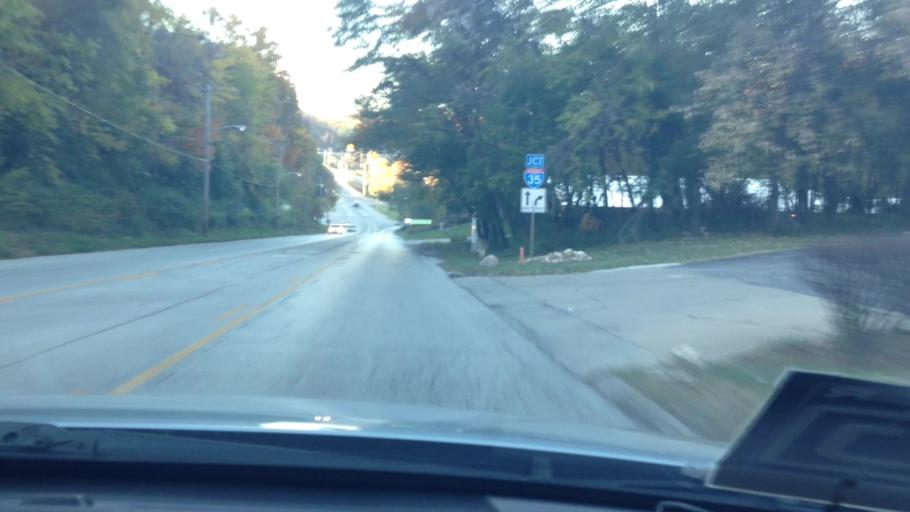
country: US
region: Kansas
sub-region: Johnson County
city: Westwood
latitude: 39.0548
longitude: -94.6221
